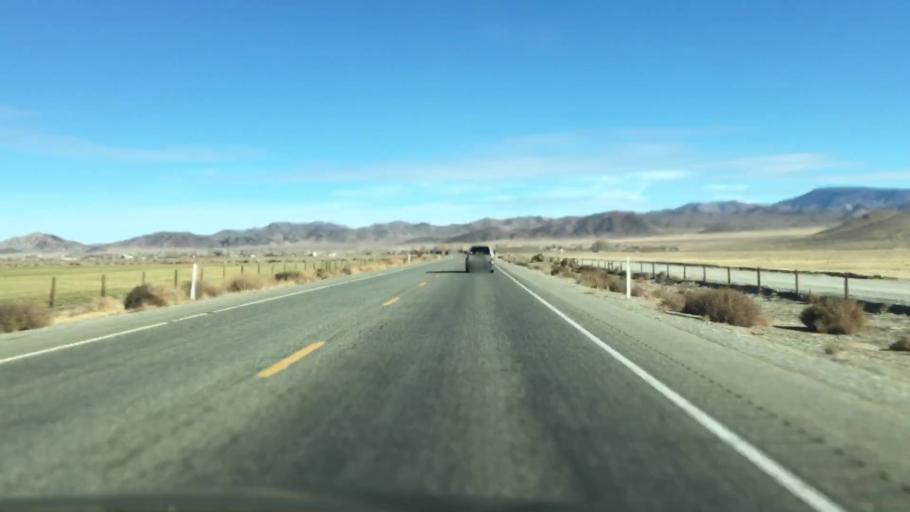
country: US
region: Nevada
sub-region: Lyon County
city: Yerington
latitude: 38.9975
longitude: -119.1104
